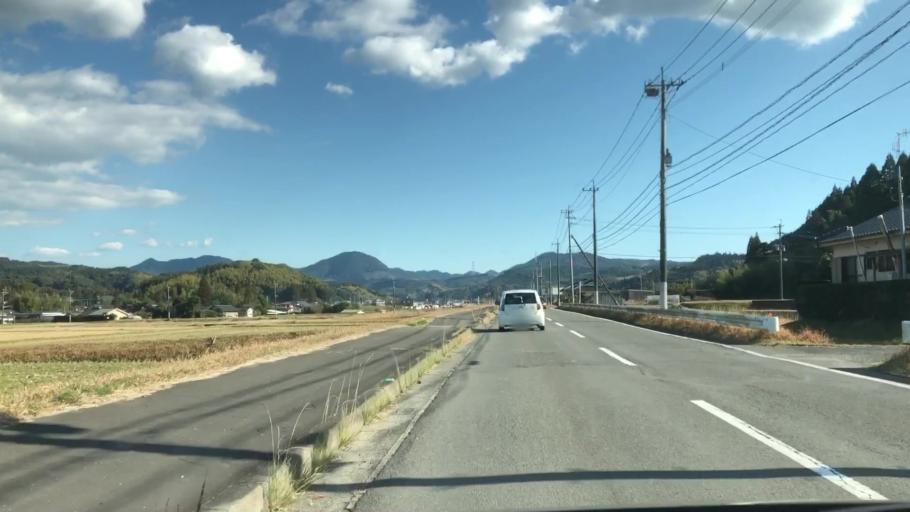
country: JP
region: Kagoshima
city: Satsumasendai
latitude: 31.7975
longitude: 130.4343
